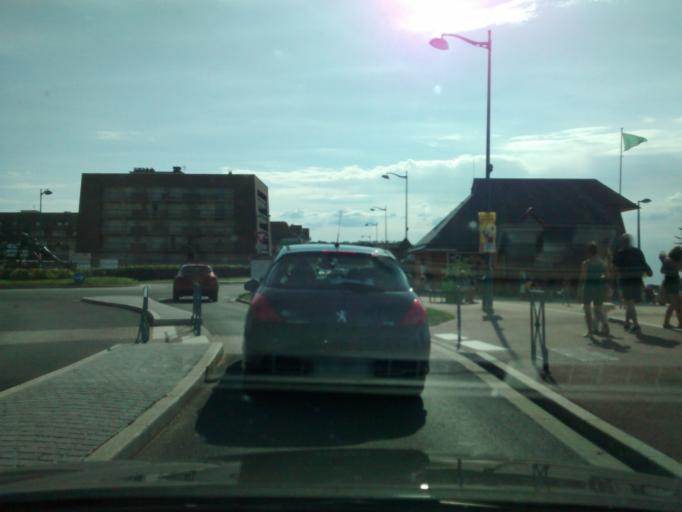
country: FR
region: Lower Normandy
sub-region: Departement du Calvados
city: Villers-sur-Mer
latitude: 49.3305
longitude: 0.0108
